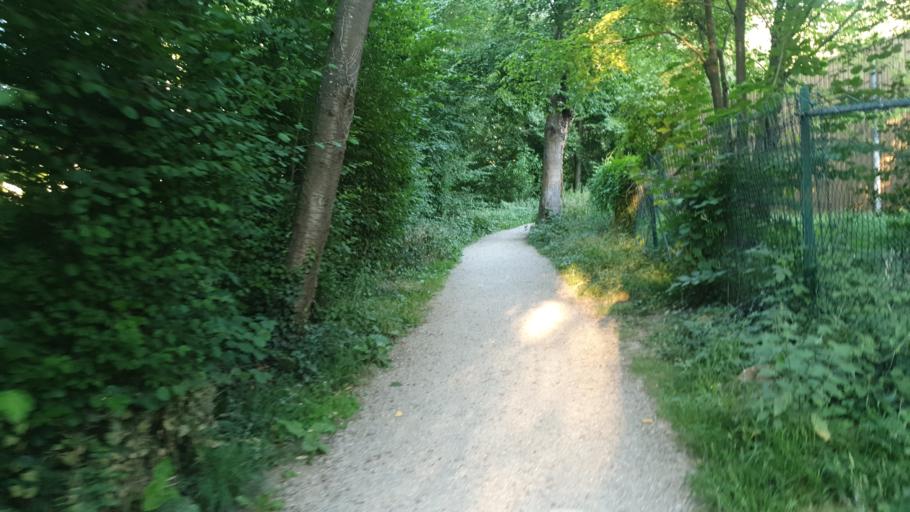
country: DE
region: Baden-Wuerttemberg
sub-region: Freiburg Region
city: Merzhausen
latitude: 47.9725
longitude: 7.8259
